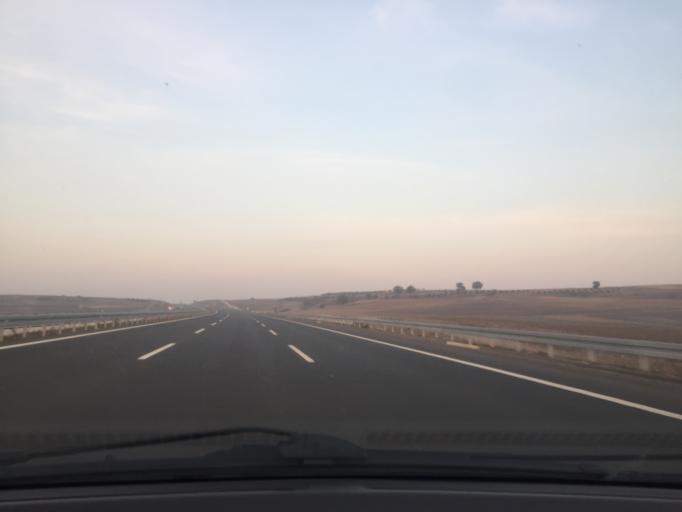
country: TR
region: Bursa
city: Mahmudiye
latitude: 40.2690
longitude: 28.6327
